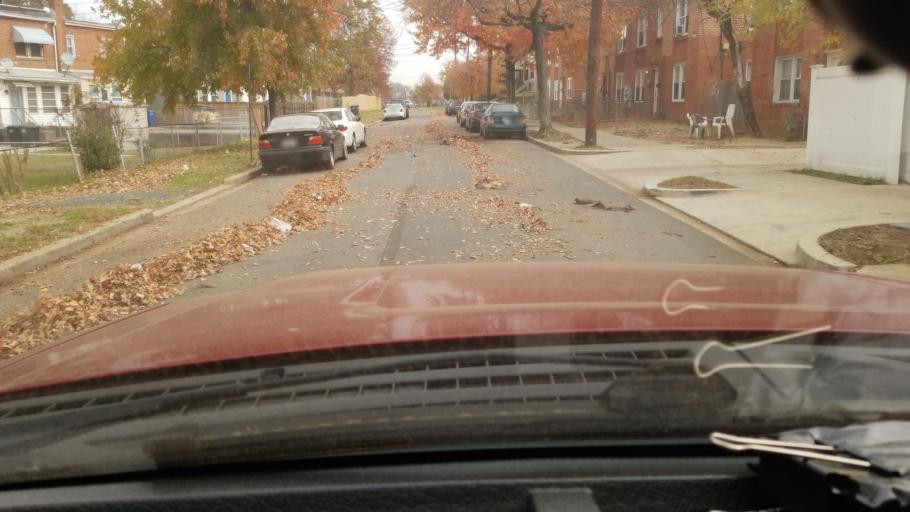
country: US
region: Maryland
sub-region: Prince George's County
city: Capitol Heights
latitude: 38.8867
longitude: -76.9252
